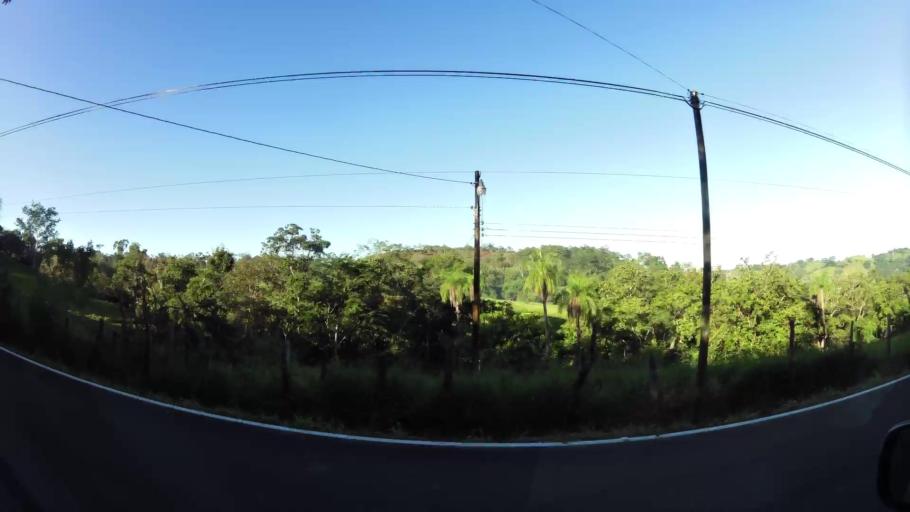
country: CR
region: Puntarenas
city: Miramar
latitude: 10.1694
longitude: -84.8513
